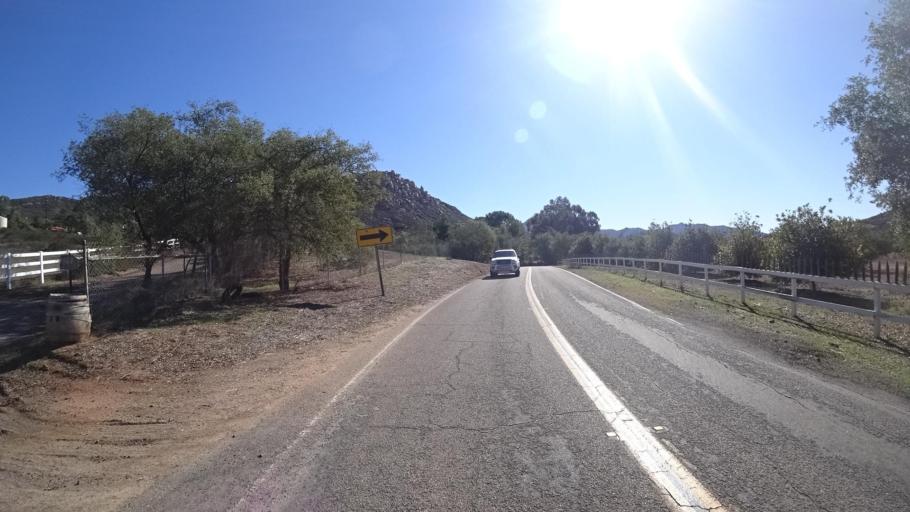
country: US
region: California
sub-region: San Diego County
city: Jamul
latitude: 32.7225
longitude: -116.8067
